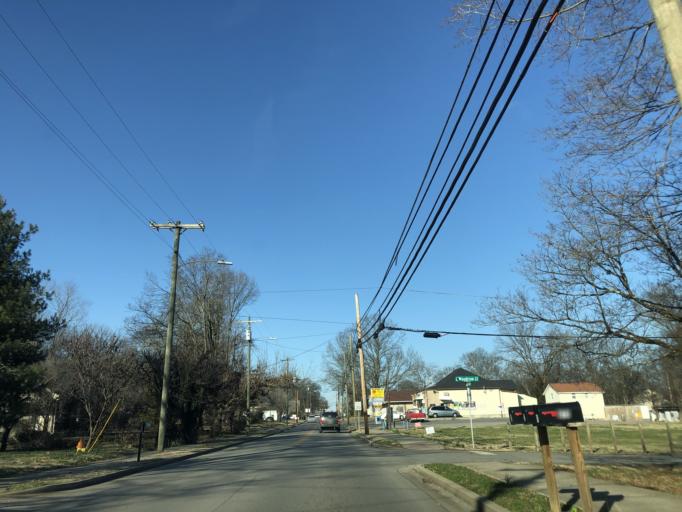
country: US
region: Tennessee
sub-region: Sumner County
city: Gallatin
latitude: 36.4002
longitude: -86.4458
